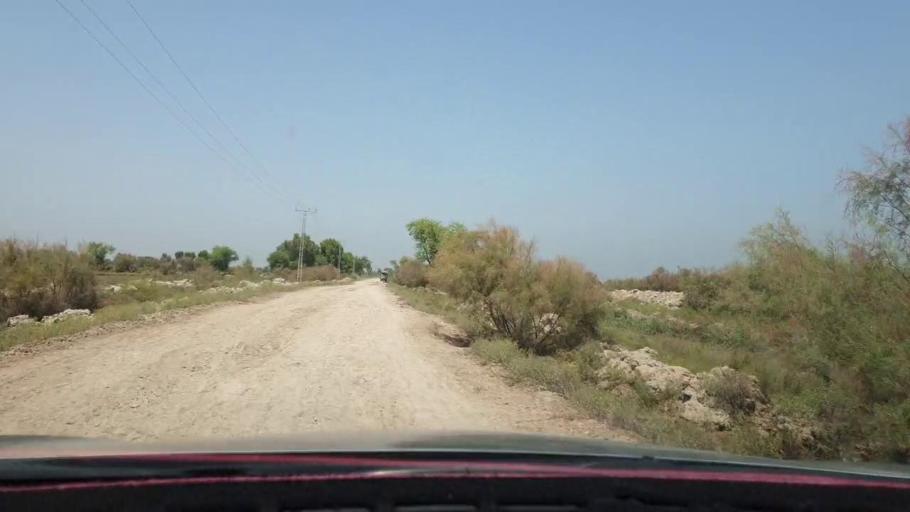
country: PK
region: Sindh
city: Warah
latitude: 27.4138
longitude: 67.6984
